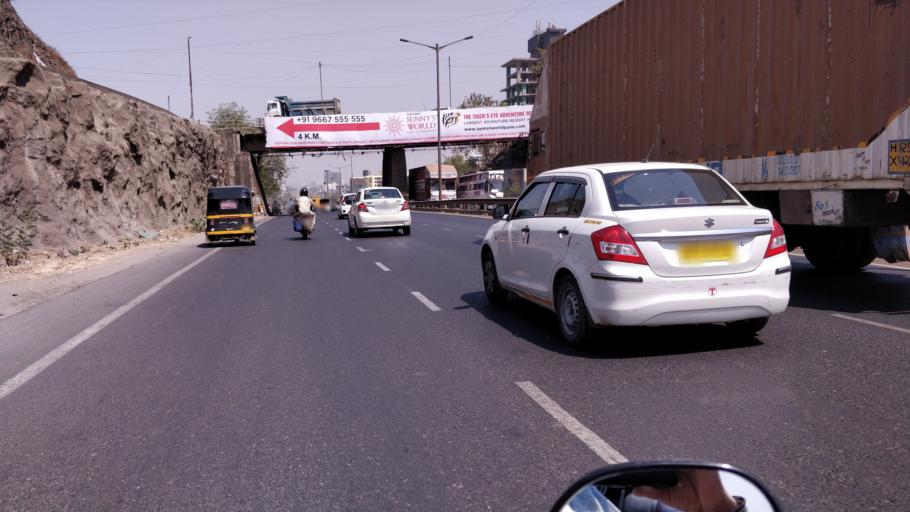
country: IN
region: Maharashtra
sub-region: Pune Division
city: Khadki
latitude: 18.5460
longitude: 73.7739
